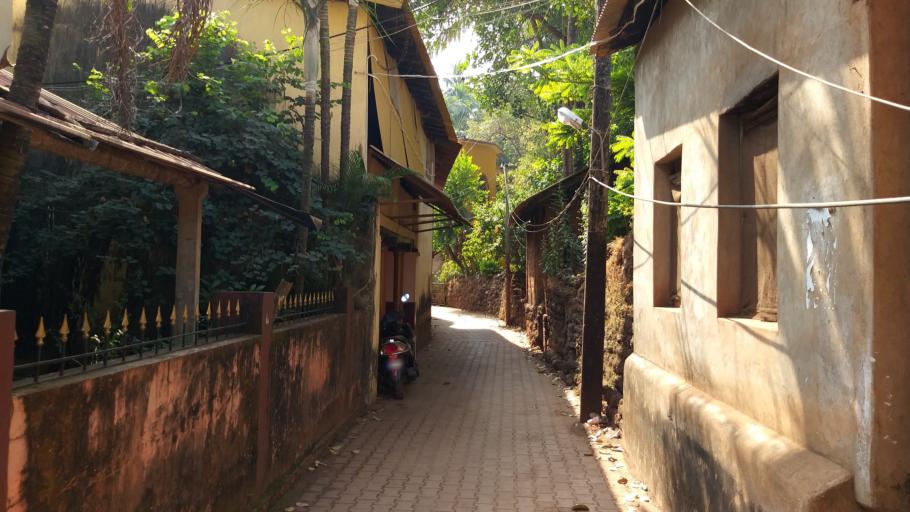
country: IN
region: Karnataka
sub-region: Uttar Kannada
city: Gokarna
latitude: 14.5430
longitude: 74.3171
